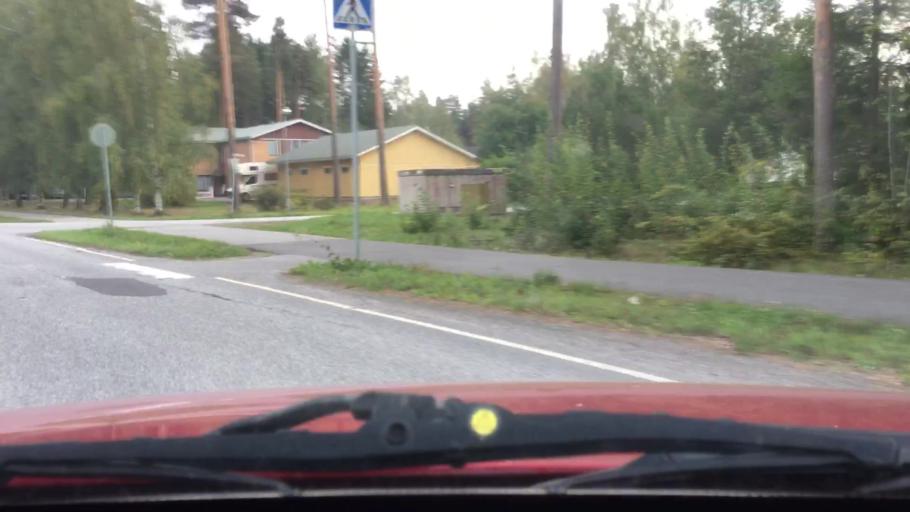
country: FI
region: Varsinais-Suomi
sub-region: Turku
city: Masku
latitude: 60.5558
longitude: 22.1280
